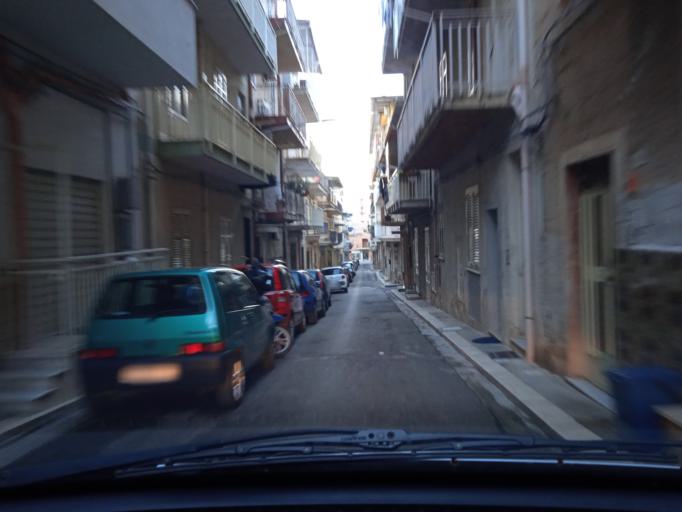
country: IT
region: Sicily
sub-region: Palermo
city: Villabate
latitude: 38.0740
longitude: 13.4481
